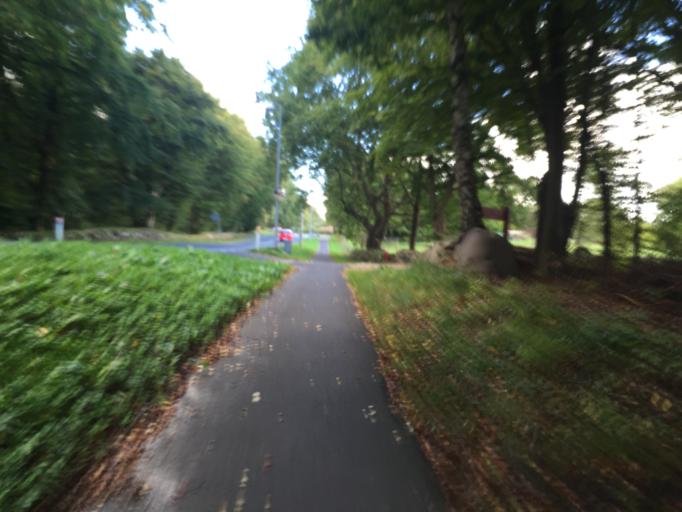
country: DK
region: Capital Region
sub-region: Fureso Kommune
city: Vaerlose
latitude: 55.7718
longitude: 12.3883
